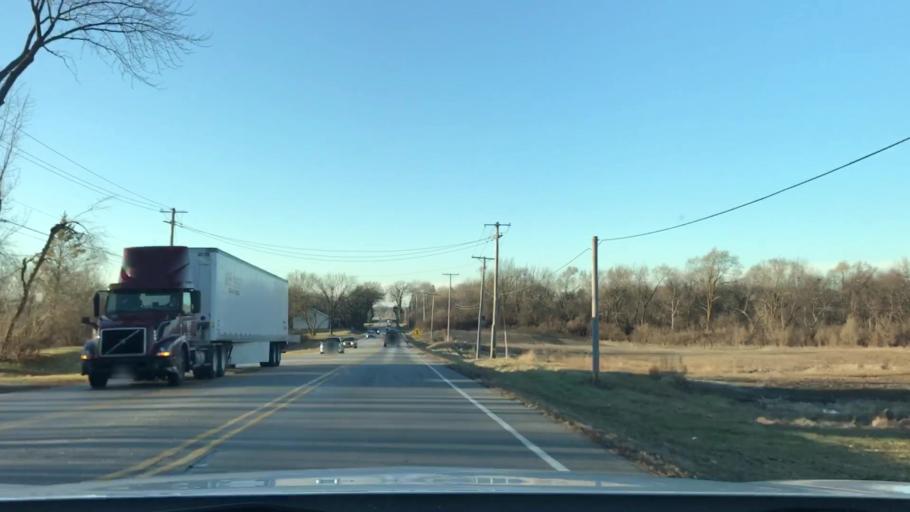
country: US
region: Illinois
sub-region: Kane County
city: Gilberts
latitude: 42.0801
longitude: -88.3813
